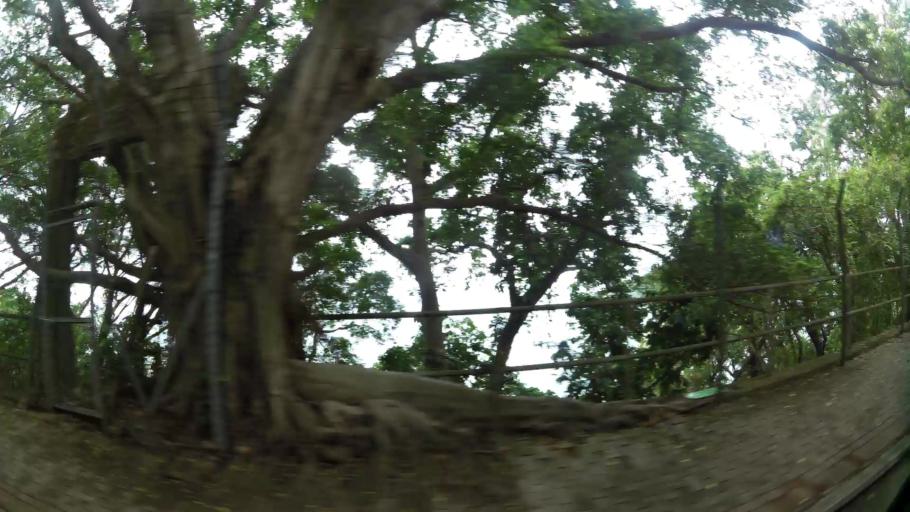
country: HK
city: Hong Kong
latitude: 22.2787
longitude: 114.1177
